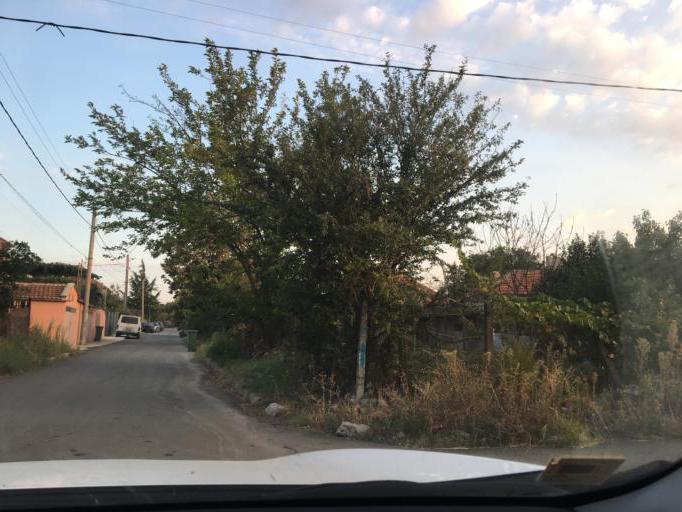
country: BG
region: Burgas
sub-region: Obshtina Burgas
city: Burgas
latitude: 42.6127
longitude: 27.4956
